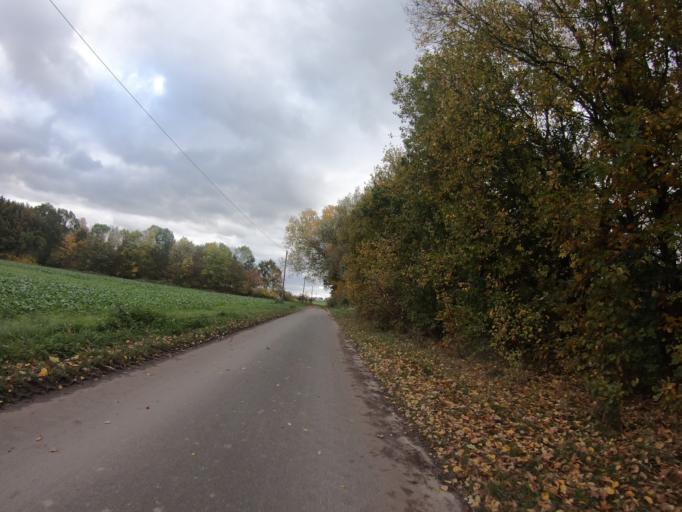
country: DE
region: Lower Saxony
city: Adenbuettel
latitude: 52.3853
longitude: 10.4851
